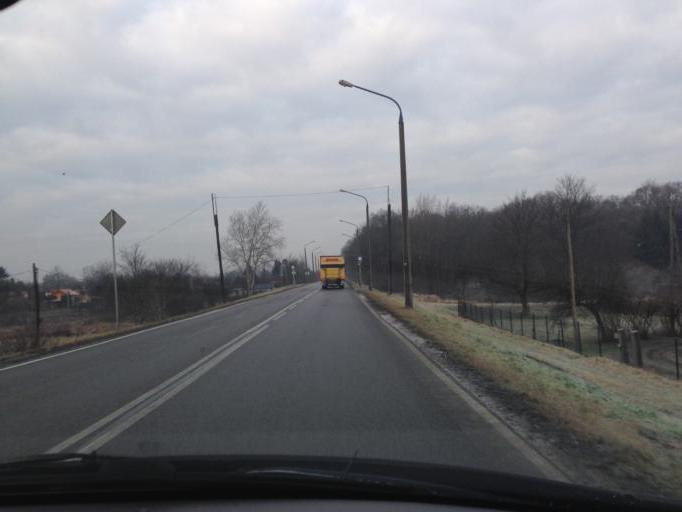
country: PL
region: Lesser Poland Voivodeship
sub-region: Powiat wielicki
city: Kokotow
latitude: 50.0530
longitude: 20.0636
